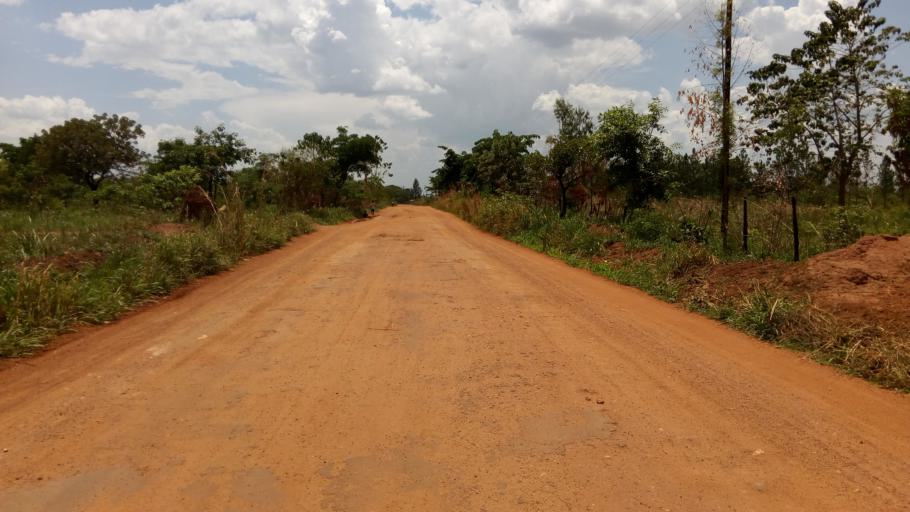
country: UG
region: Northern Region
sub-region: Gulu District
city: Gulu
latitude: 2.7858
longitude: 32.3523
